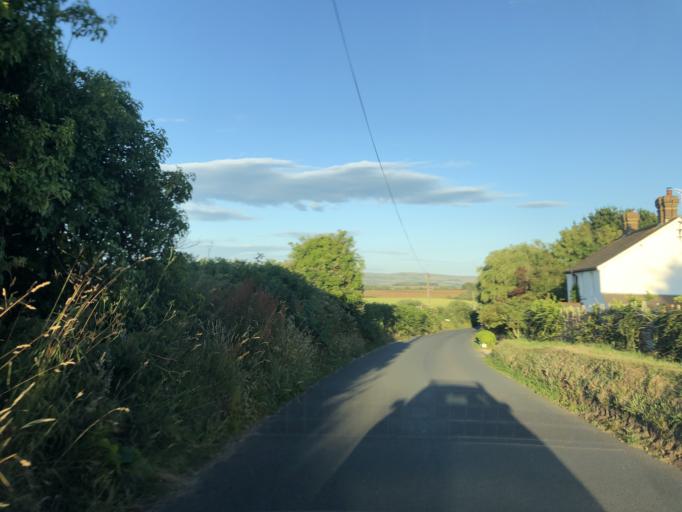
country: GB
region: England
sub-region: Isle of Wight
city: Chale
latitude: 50.6351
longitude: -1.3314
